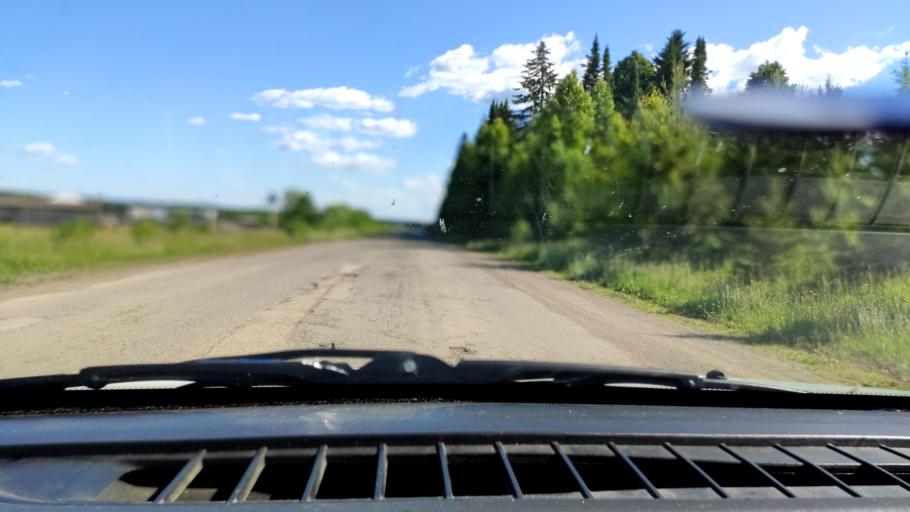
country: RU
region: Perm
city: Uinskoye
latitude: 57.1750
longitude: 56.5609
